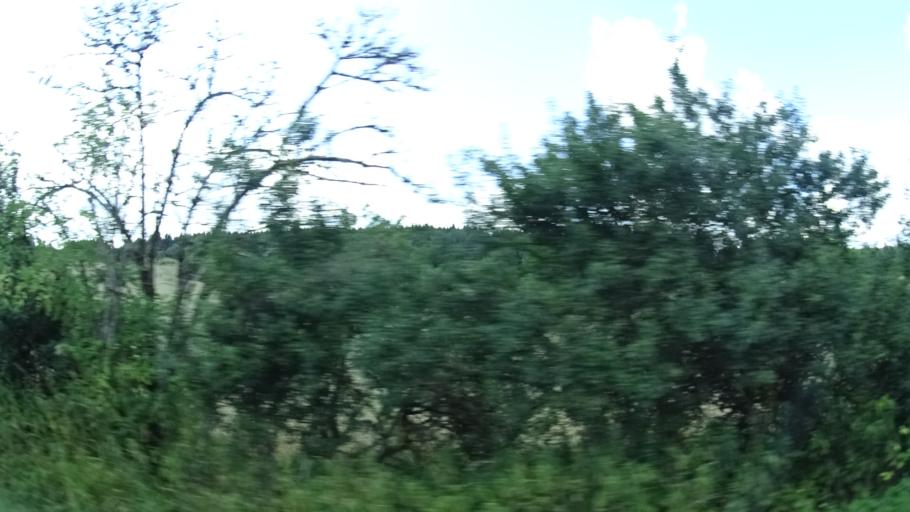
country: DE
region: Thuringia
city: Veilsdorf
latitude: 50.3988
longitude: 10.7886
